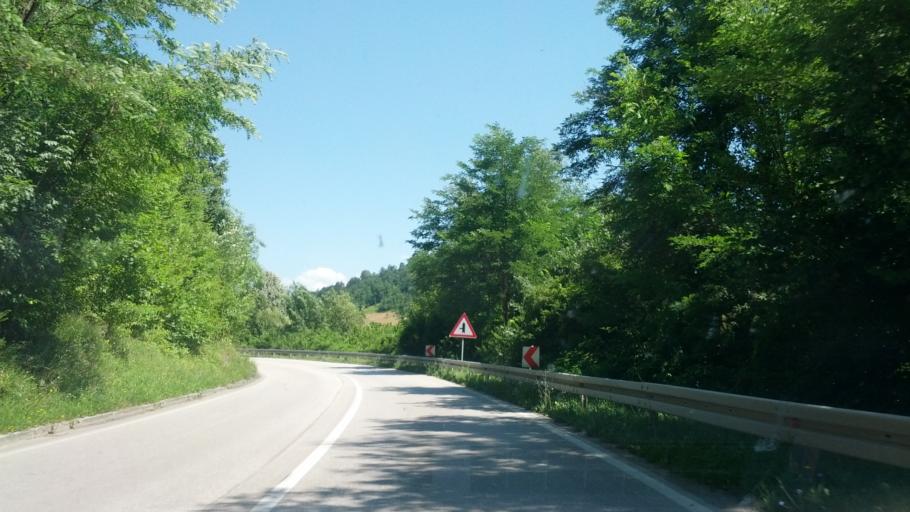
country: BA
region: Federation of Bosnia and Herzegovina
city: Bosanska Krupa
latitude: 44.9213
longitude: 16.1461
